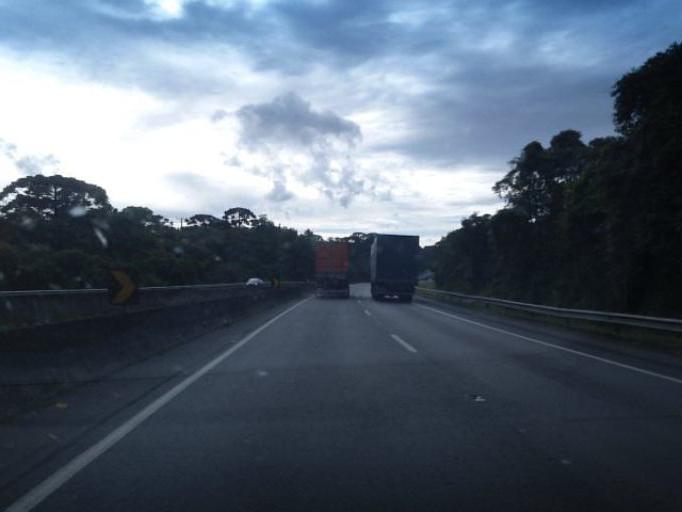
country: BR
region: Parana
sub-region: Campina Grande Do Sul
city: Campina Grande do Sul
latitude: -25.3080
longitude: -48.9816
